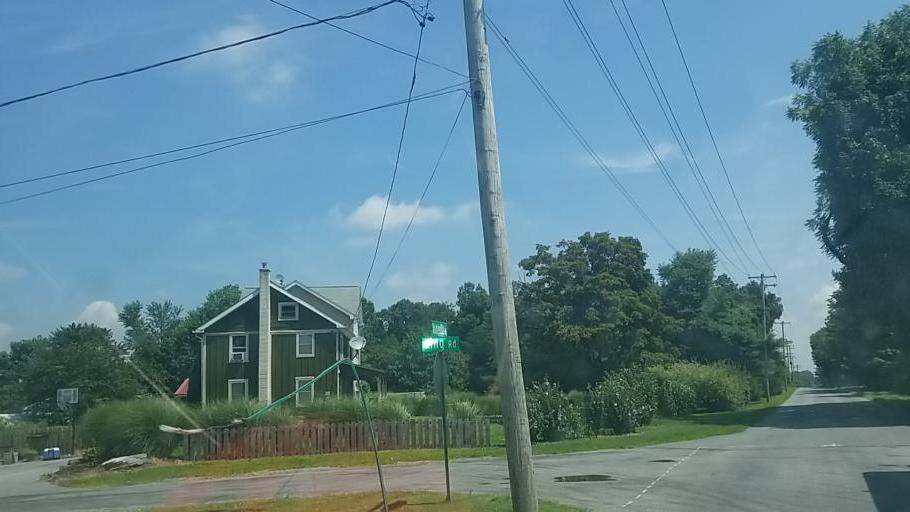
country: US
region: Pennsylvania
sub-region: Chester County
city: Atglen
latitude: 39.8872
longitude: -75.9559
